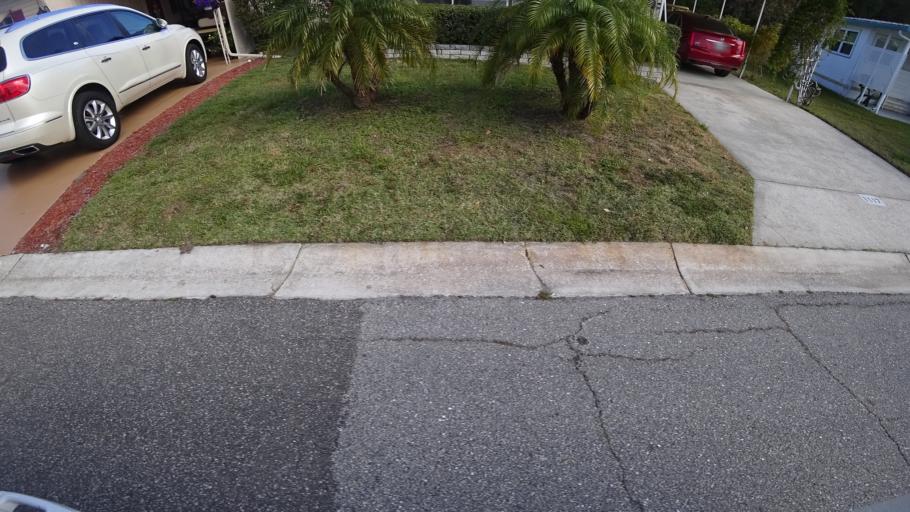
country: US
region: Florida
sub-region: Manatee County
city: Ellenton
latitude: 27.5239
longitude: -82.5178
